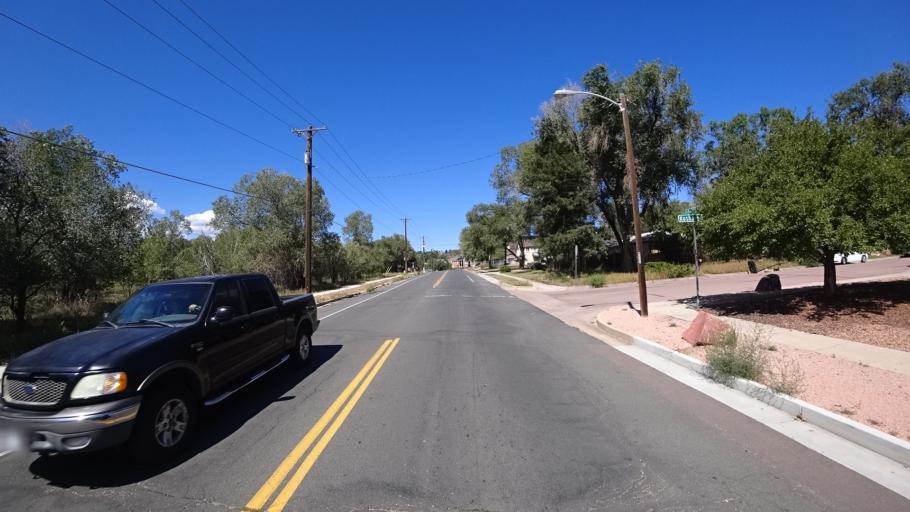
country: US
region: Colorado
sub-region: El Paso County
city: Colorado Springs
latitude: 38.8548
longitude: -104.8497
